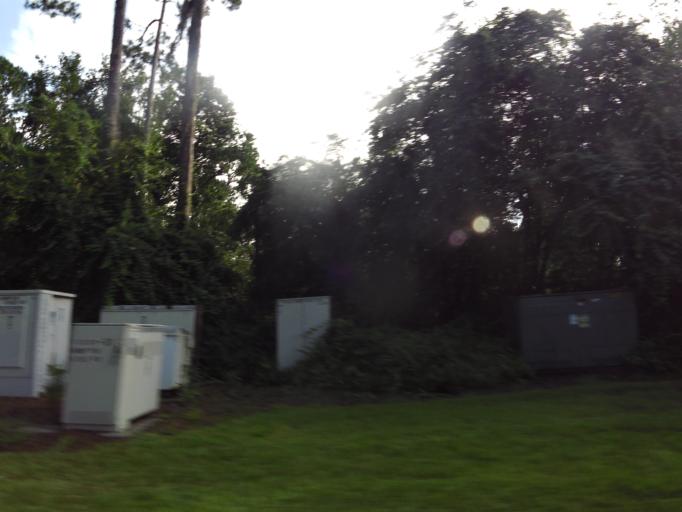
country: US
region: Florida
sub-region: Saint Johns County
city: Fruit Cove
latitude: 30.2121
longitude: -81.5386
